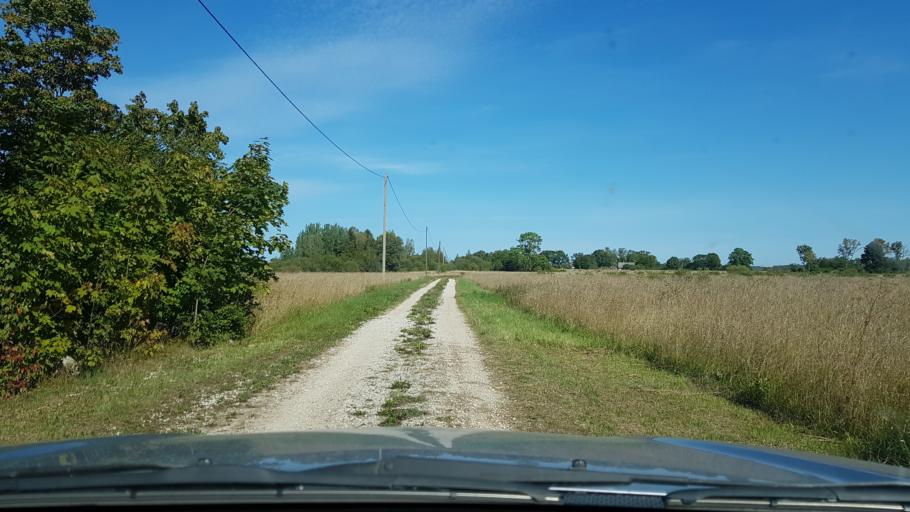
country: EE
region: Ida-Virumaa
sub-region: Sillamaee linn
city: Sillamae
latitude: 59.3797
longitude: 27.8069
